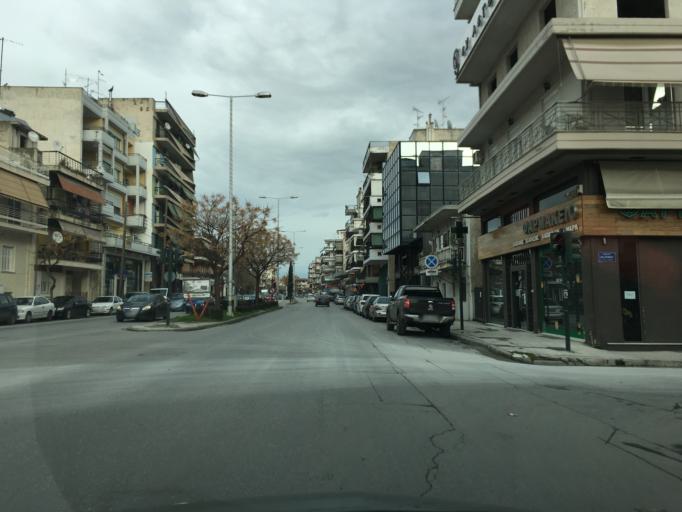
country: GR
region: Thessaly
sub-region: Nomos Larisis
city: Larisa
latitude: 39.6315
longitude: 22.4221
